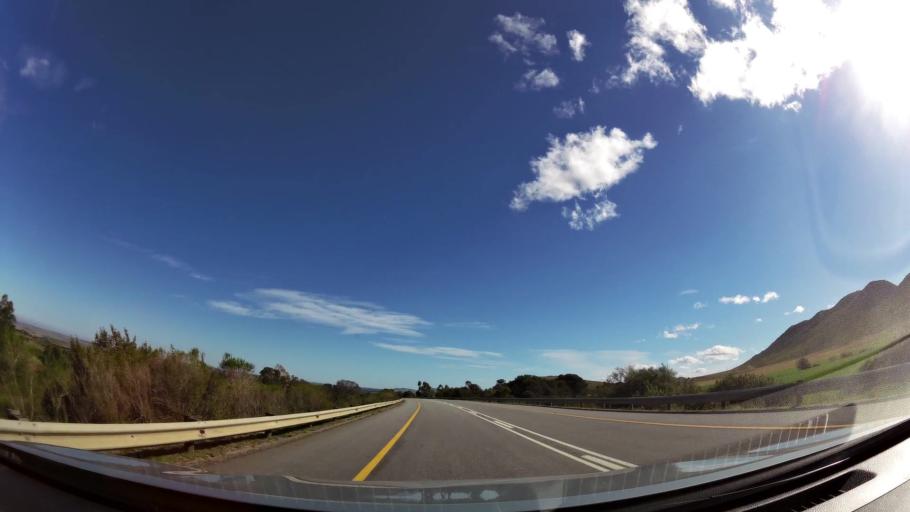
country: ZA
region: Eastern Cape
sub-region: Cacadu District Municipality
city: Kruisfontein
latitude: -33.9942
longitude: 24.6948
